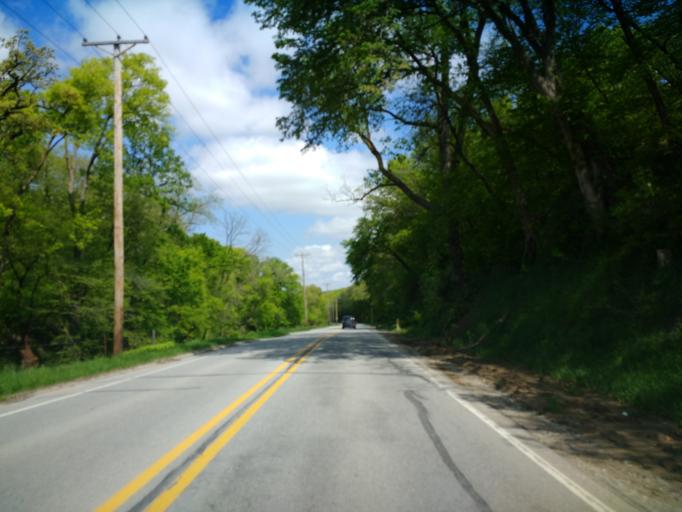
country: US
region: Iowa
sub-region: Harrison County
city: Missouri Valley
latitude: 41.4220
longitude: -95.8514
